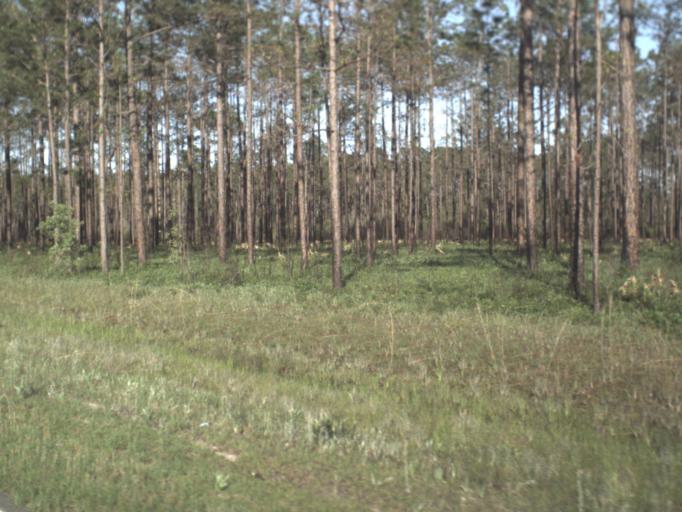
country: US
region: Florida
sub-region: Liberty County
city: Bristol
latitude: 30.1920
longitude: -84.9245
